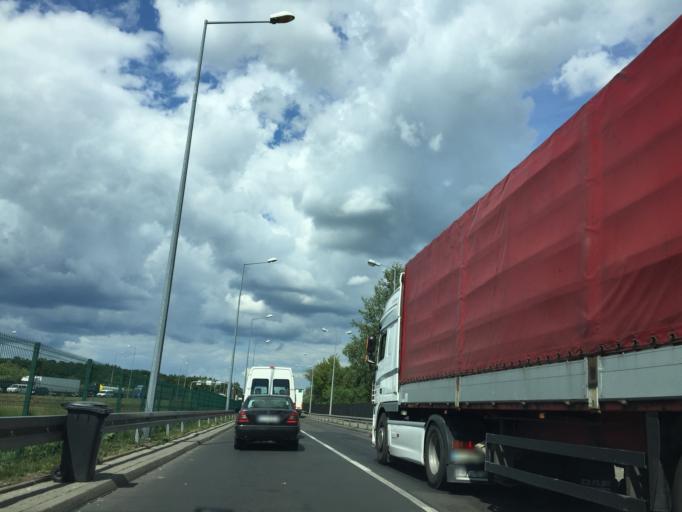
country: PL
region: Lublin Voivodeship
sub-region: Powiat chelmski
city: Dorohusk
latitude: 51.1822
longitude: 23.8051
